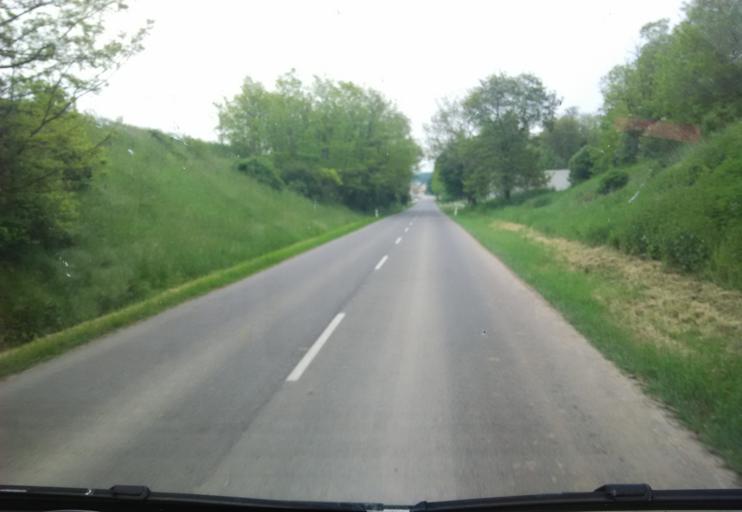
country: SK
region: Trnavsky
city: Leopoldov
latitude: 48.4606
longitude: 17.7098
